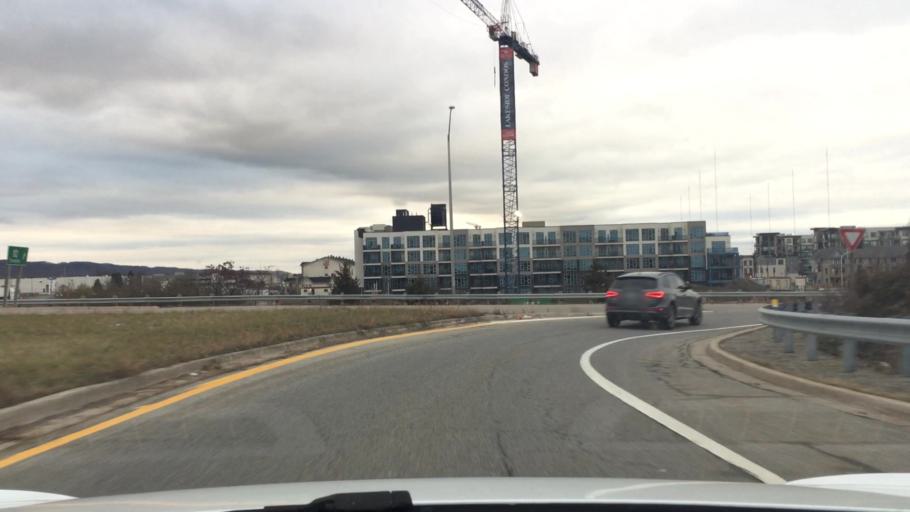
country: CA
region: Ontario
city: Oakville
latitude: 43.2086
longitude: -79.5951
